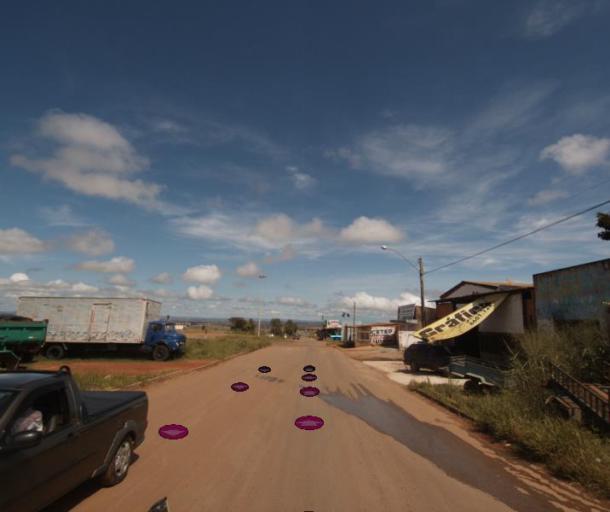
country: BR
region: Federal District
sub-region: Brasilia
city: Brasilia
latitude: -15.7374
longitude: -48.2944
